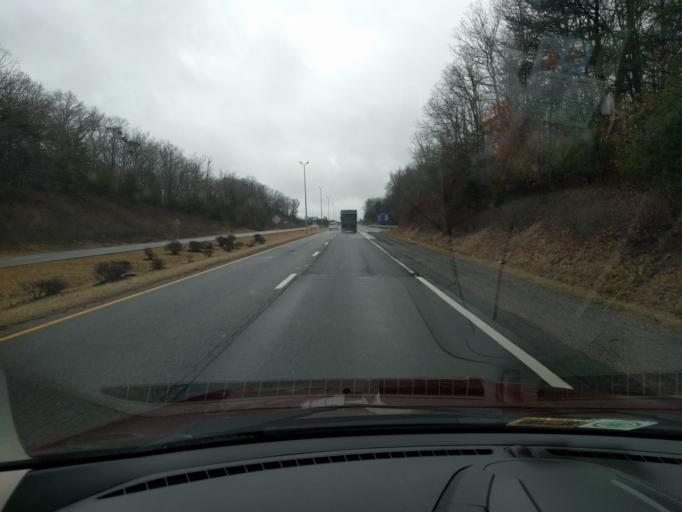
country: US
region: Virginia
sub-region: Montgomery County
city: Merrimac
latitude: 37.2014
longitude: -80.4152
